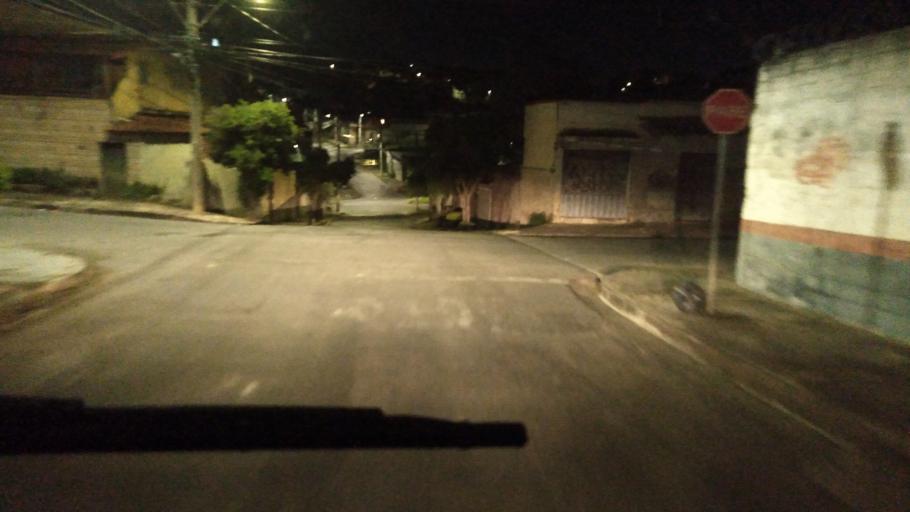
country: BR
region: Minas Gerais
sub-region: Belo Horizonte
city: Belo Horizonte
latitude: -19.8743
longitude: -43.9424
